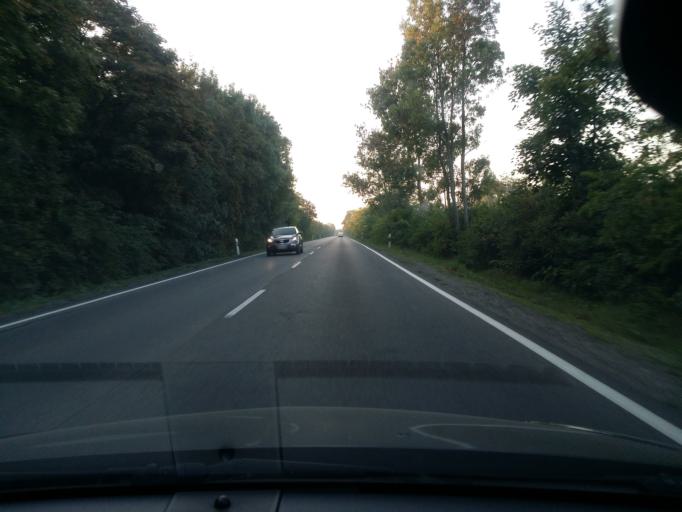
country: HU
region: Fejer
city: dunaujvaros
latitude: 46.9545
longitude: 18.9114
